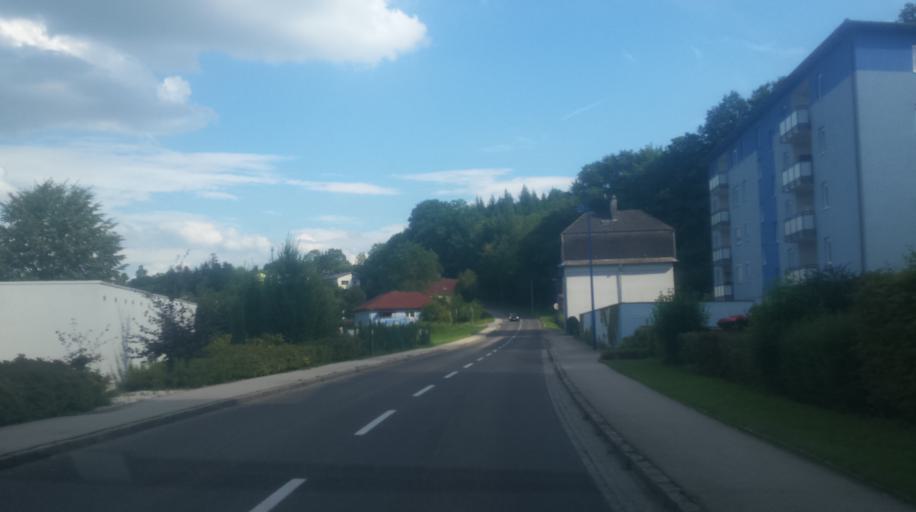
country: AT
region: Upper Austria
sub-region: Politischer Bezirk Grieskirchen
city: Bad Schallerbach
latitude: 48.2256
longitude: 13.9277
